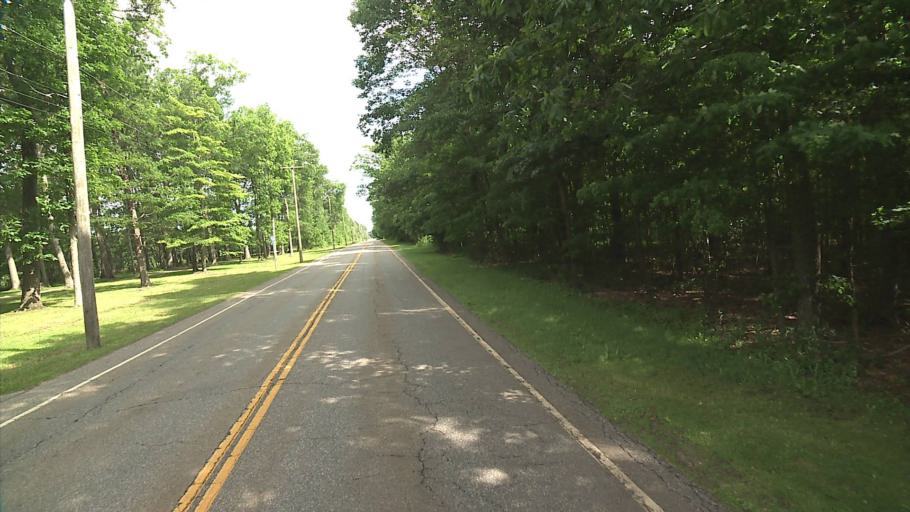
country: US
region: Connecticut
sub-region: Litchfield County
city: Litchfield
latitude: 41.8007
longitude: -73.2134
